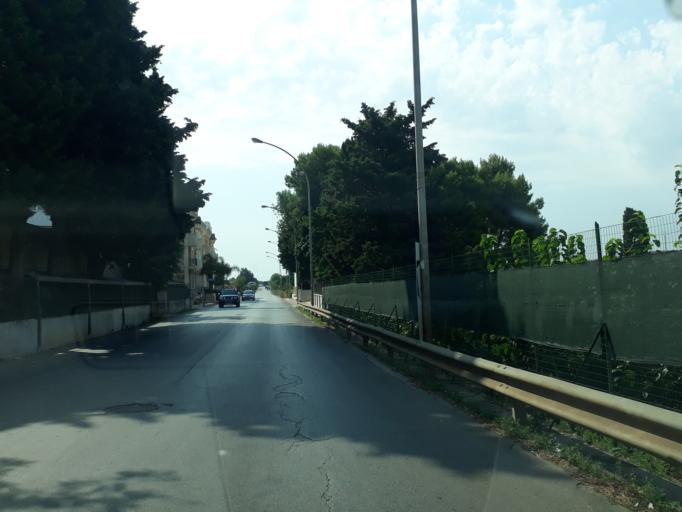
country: IT
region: Apulia
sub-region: Provincia di Brindisi
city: Carovigno
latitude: 40.6998
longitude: 17.6645
